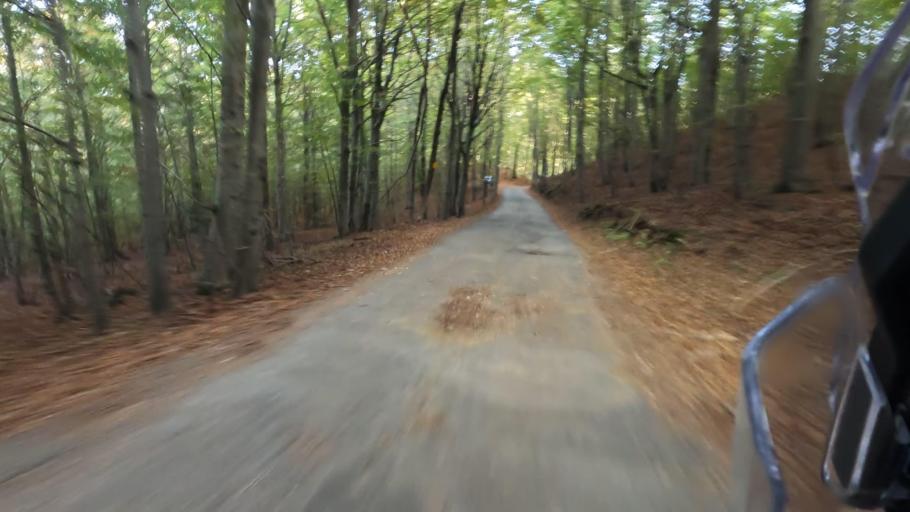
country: IT
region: Liguria
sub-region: Provincia di Savona
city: Urbe
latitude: 44.4409
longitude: 8.5803
